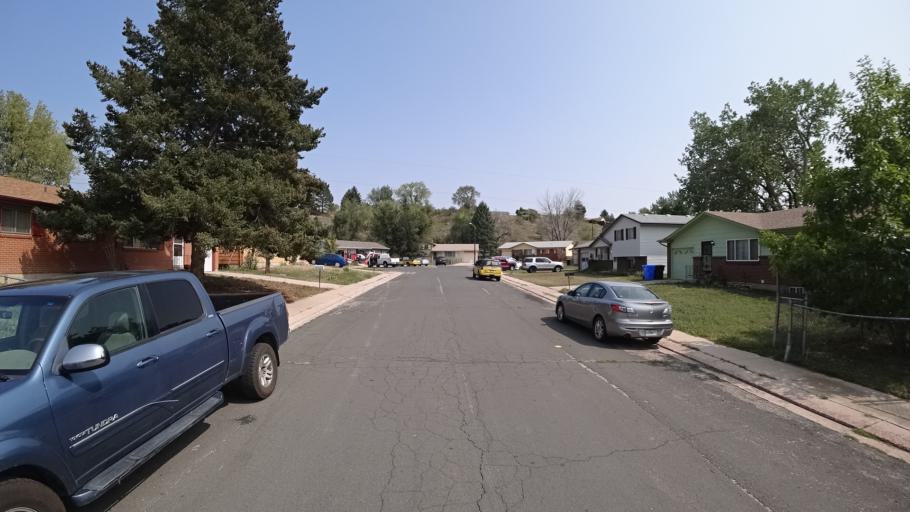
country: US
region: Colorado
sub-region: El Paso County
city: Stratmoor
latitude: 38.7979
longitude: -104.7743
